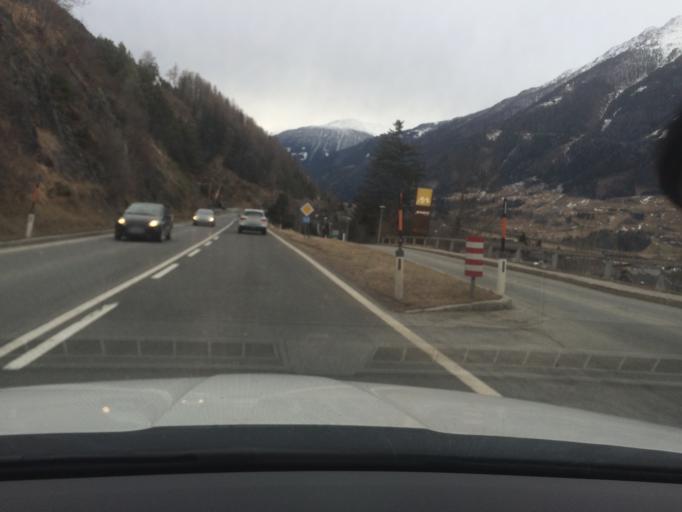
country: AT
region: Tyrol
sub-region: Politischer Bezirk Lienz
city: Matrei in Osttirol
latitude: 47.0052
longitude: 12.5410
